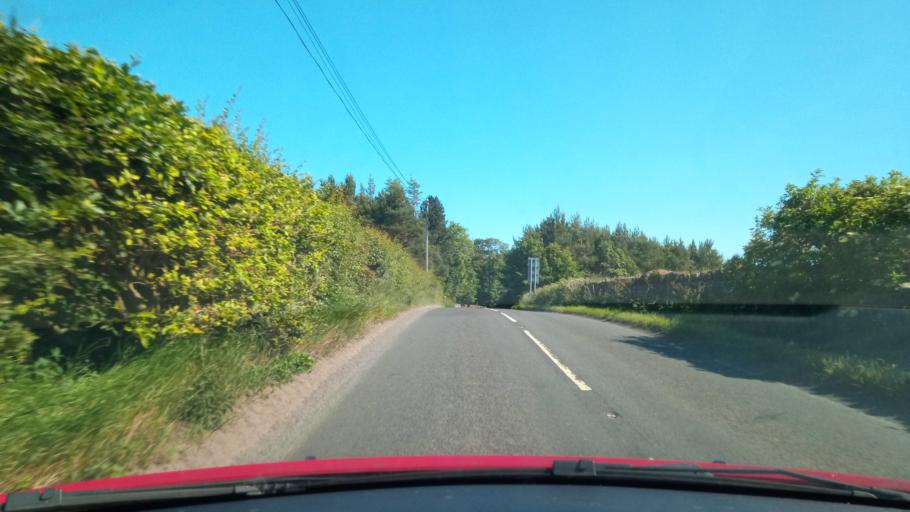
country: GB
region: Scotland
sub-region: East Lothian
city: East Linton
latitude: 56.0368
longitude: -2.6397
